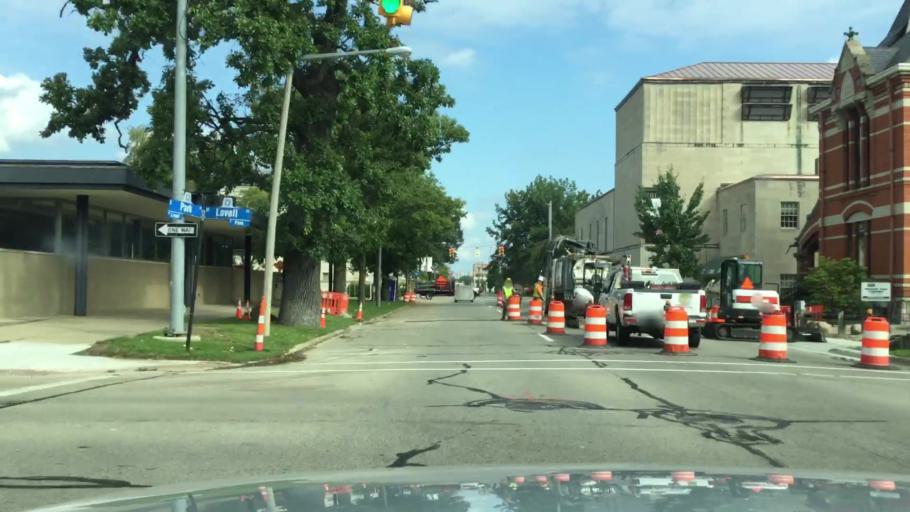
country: US
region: Michigan
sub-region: Kalamazoo County
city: Kalamazoo
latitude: 42.2887
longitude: -85.5873
